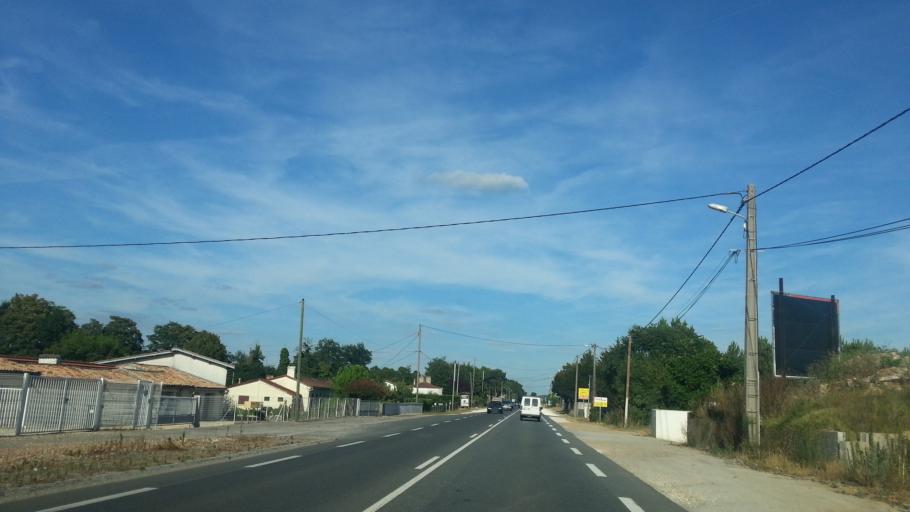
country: FR
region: Aquitaine
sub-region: Departement de la Gironde
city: Ayguemorte-les-Graves
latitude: 44.6960
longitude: -0.4861
